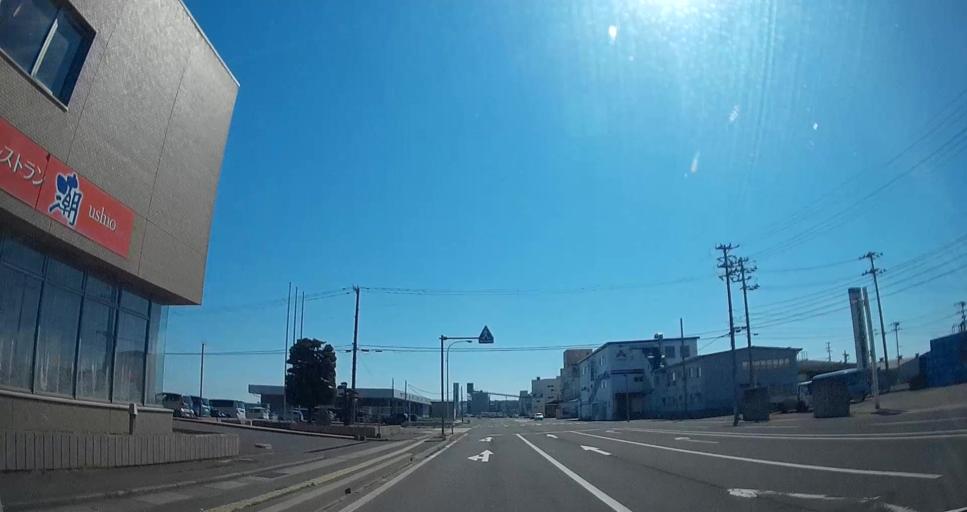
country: JP
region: Aomori
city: Hachinohe
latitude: 40.5264
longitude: 141.5357
